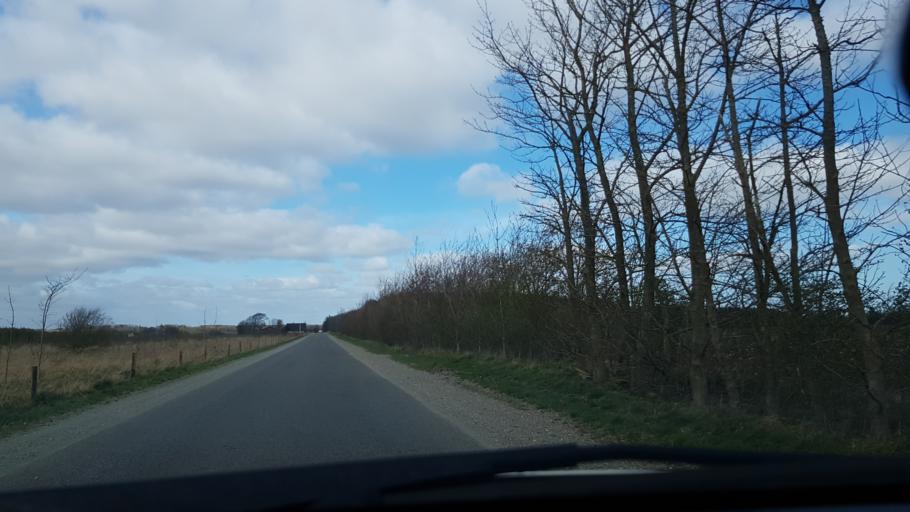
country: DK
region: South Denmark
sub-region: Vejen Kommune
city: Rodding
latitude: 55.3701
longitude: 8.9944
